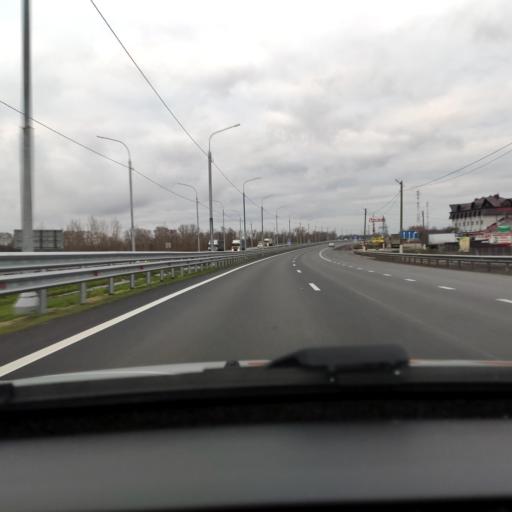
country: RU
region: Voronezj
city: Ramon'
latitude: 51.9858
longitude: 39.2153
